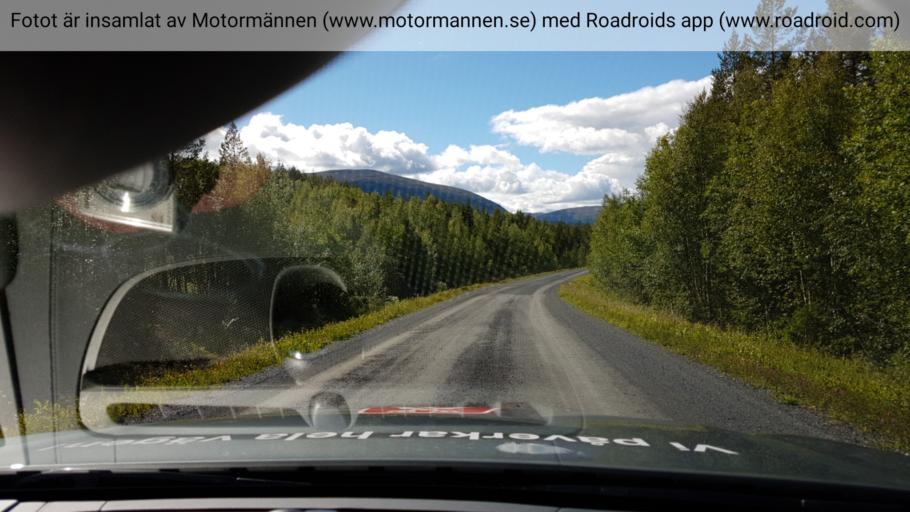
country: SE
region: Jaemtland
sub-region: Krokoms Kommun
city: Valla
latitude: 63.0810
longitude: 13.9344
